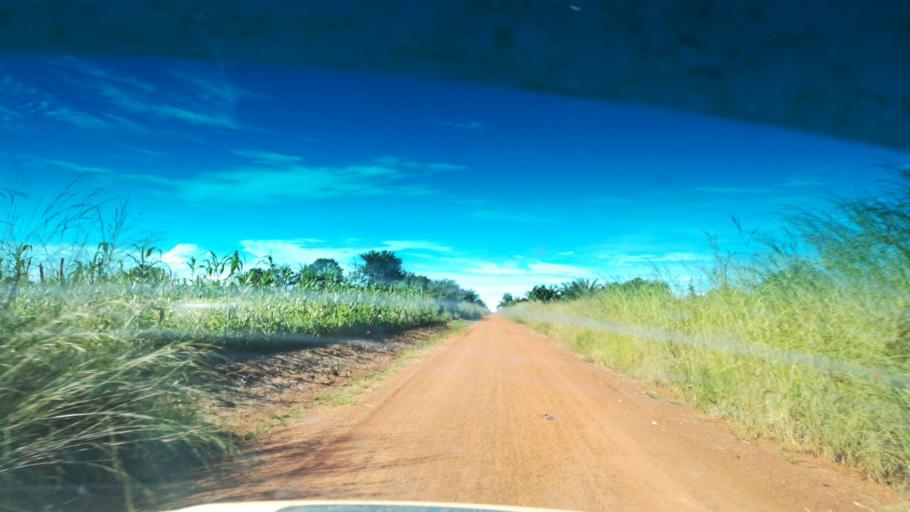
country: ZM
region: Luapula
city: Nchelenge
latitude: -9.3377
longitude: 28.2351
